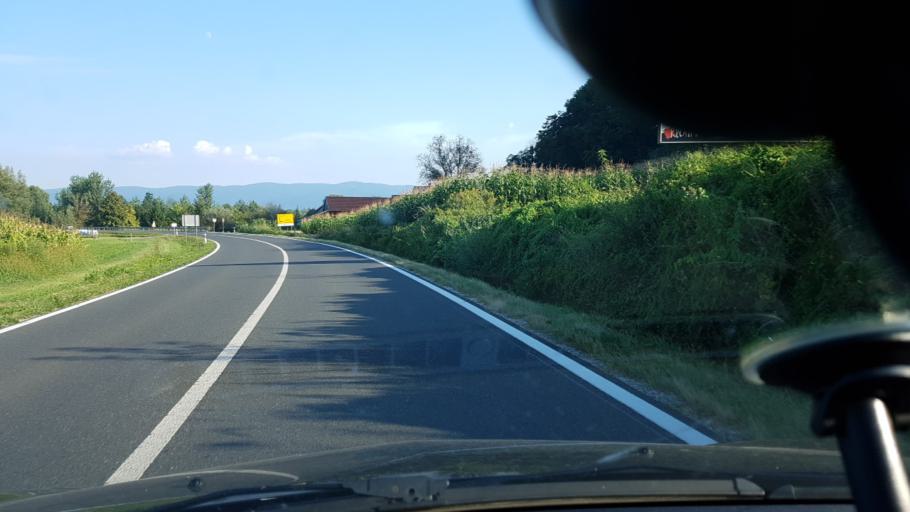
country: HR
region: Krapinsko-Zagorska
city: Zabok
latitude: 46.0214
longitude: 15.8522
